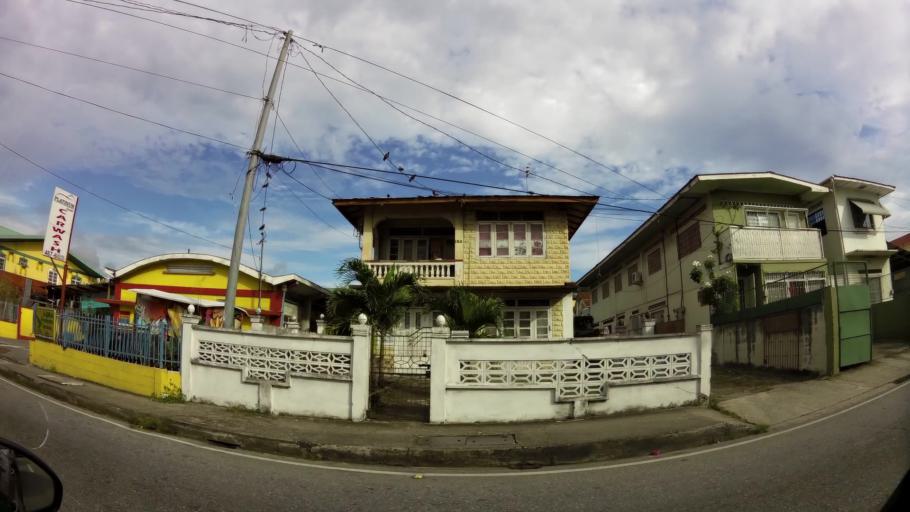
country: TT
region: San Juan/Laventille
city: Laventille
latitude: 10.6509
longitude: -61.4435
